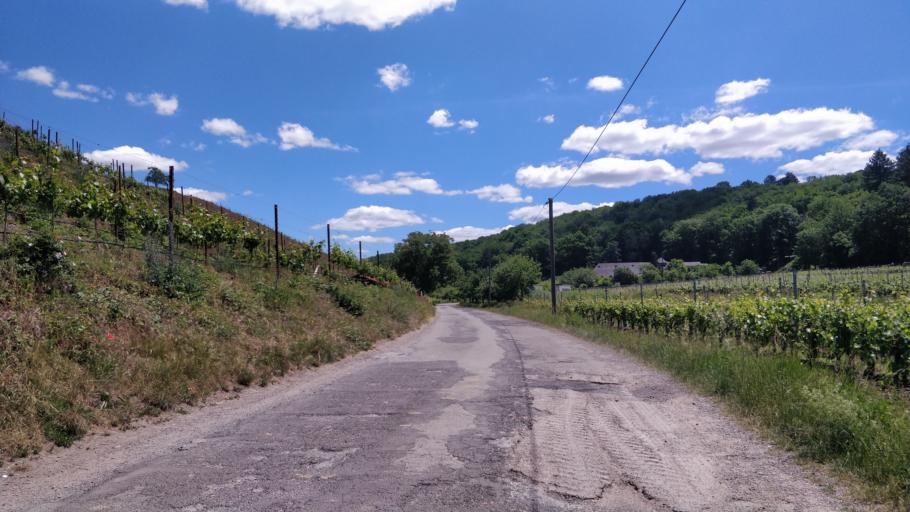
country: DE
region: Rheinland-Pfalz
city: Trier
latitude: 49.7403
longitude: 6.6554
